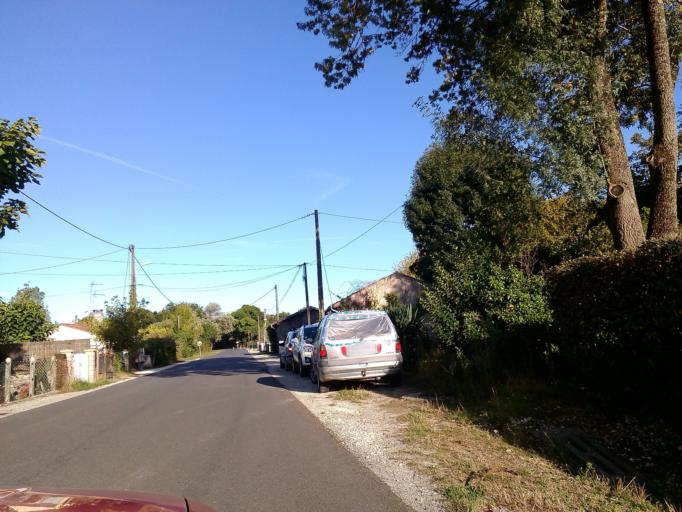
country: FR
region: Aquitaine
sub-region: Departement de la Gironde
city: Soulac-sur-Mer
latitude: 45.4293
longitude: -1.0287
